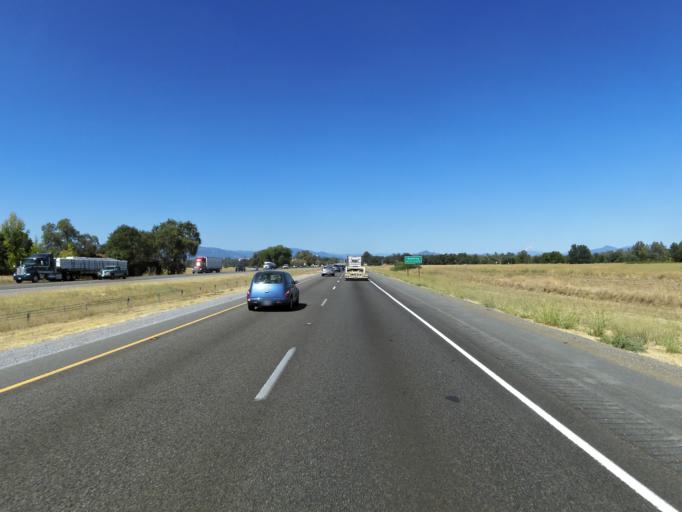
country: US
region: California
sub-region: Shasta County
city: Redding
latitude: 40.5225
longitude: -122.3458
